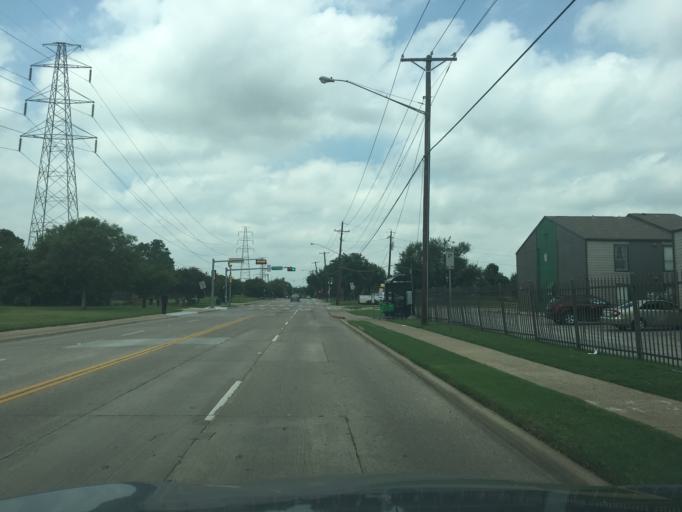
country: US
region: Texas
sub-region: Dallas County
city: Richardson
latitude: 32.9359
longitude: -96.7612
